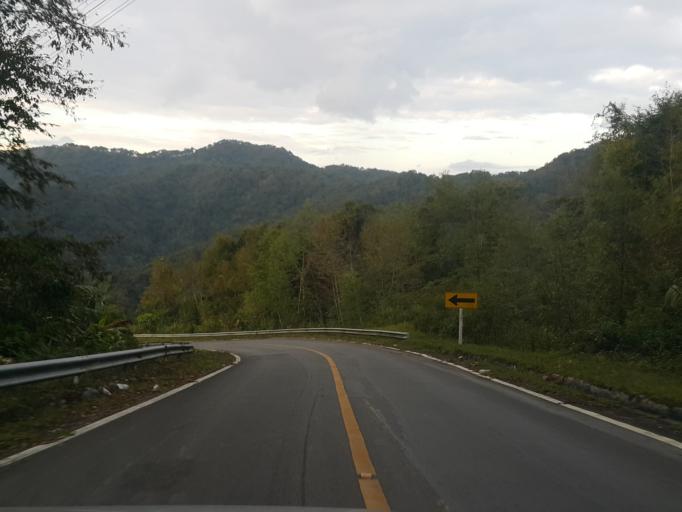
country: TH
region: Mae Hong Son
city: Khun Yuam
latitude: 18.8005
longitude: 98.0758
